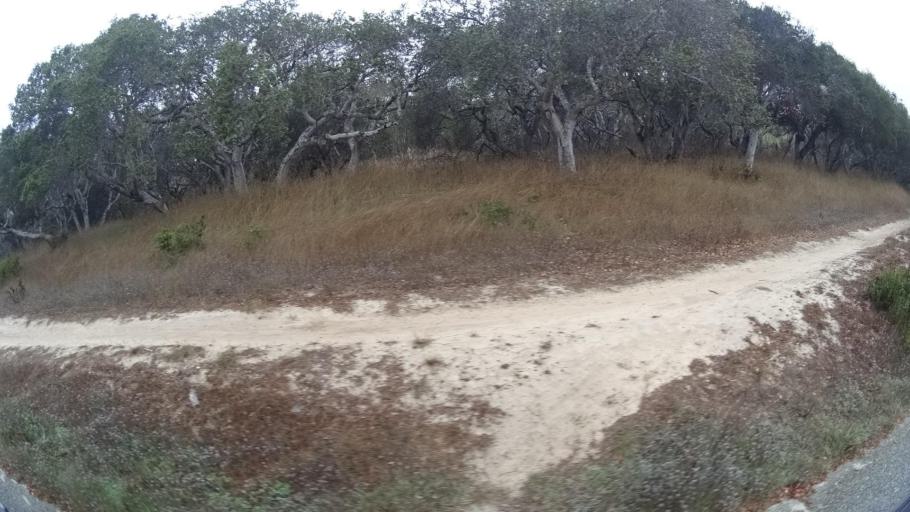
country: US
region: California
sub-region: Monterey County
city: Marina
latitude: 36.6450
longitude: -121.7712
